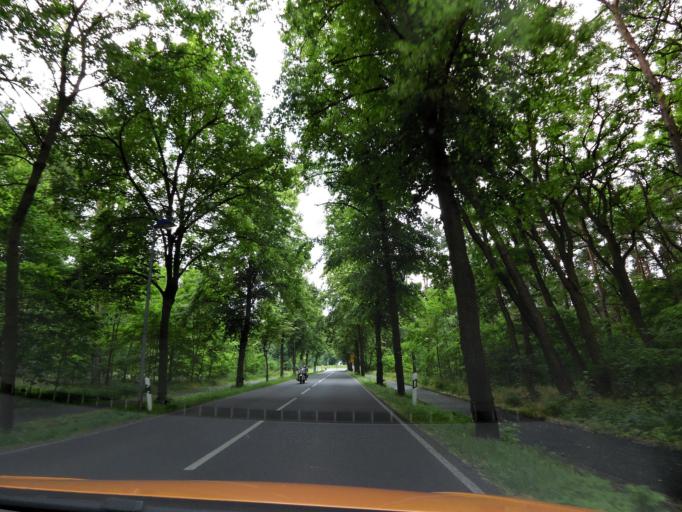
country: DE
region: Brandenburg
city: Zossen
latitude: 52.1768
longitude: 13.4682
